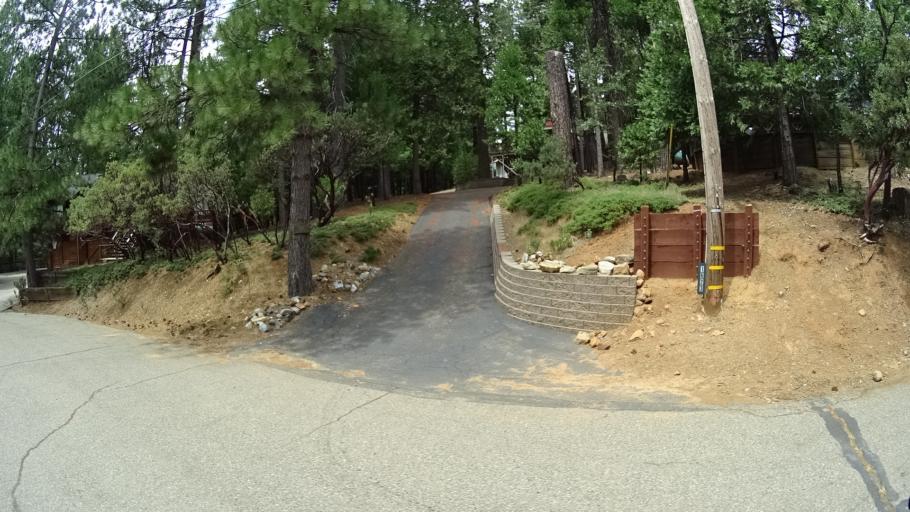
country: US
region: California
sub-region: Calaveras County
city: Arnold
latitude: 38.2354
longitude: -120.3585
